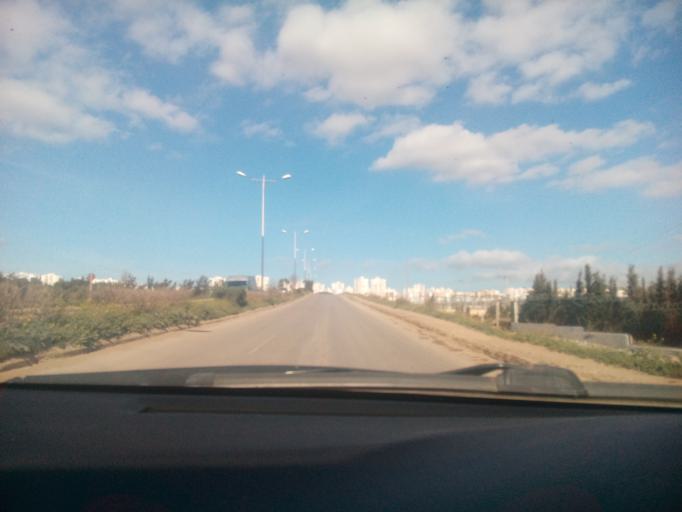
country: DZ
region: Oran
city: Bir el Djir
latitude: 35.6899
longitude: -0.5754
